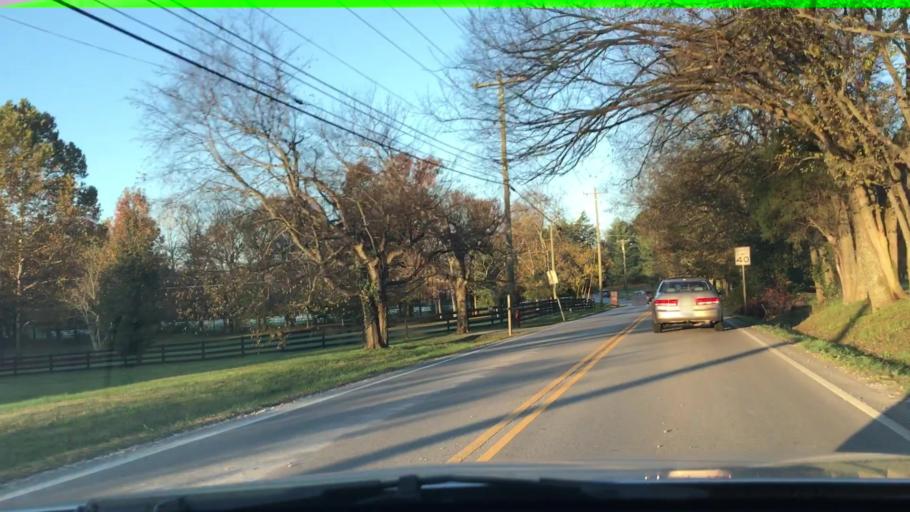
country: US
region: Tennessee
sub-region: Williamson County
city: Brentwood Estates
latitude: 36.0149
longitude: -86.7277
